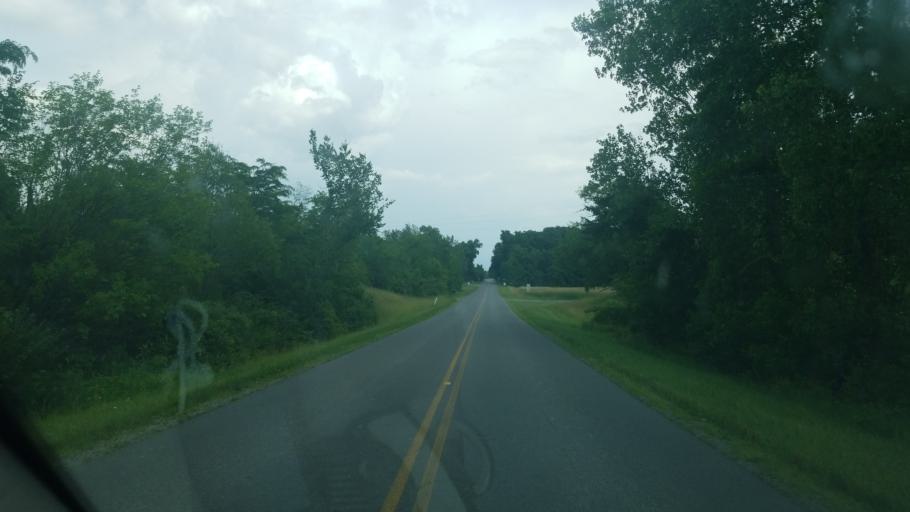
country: US
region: Ohio
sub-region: Logan County
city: Northwood
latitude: 40.4648
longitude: -83.6855
